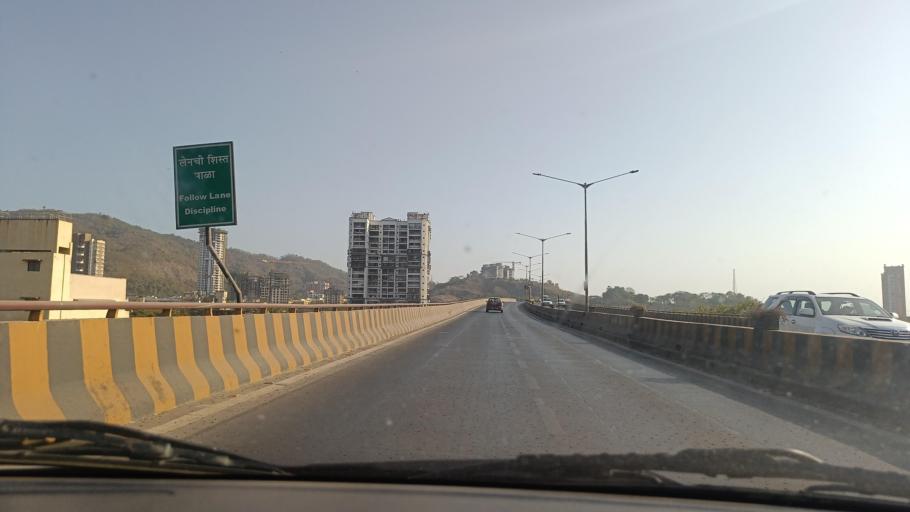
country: IN
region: Maharashtra
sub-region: Mumbai Suburban
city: Mumbai
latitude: 19.0477
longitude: 72.9098
